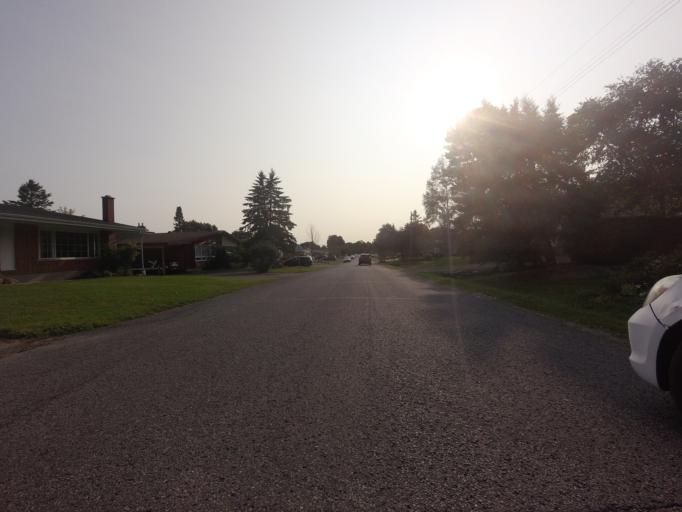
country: CA
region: Ontario
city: Ottawa
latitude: 45.3436
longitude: -75.7418
